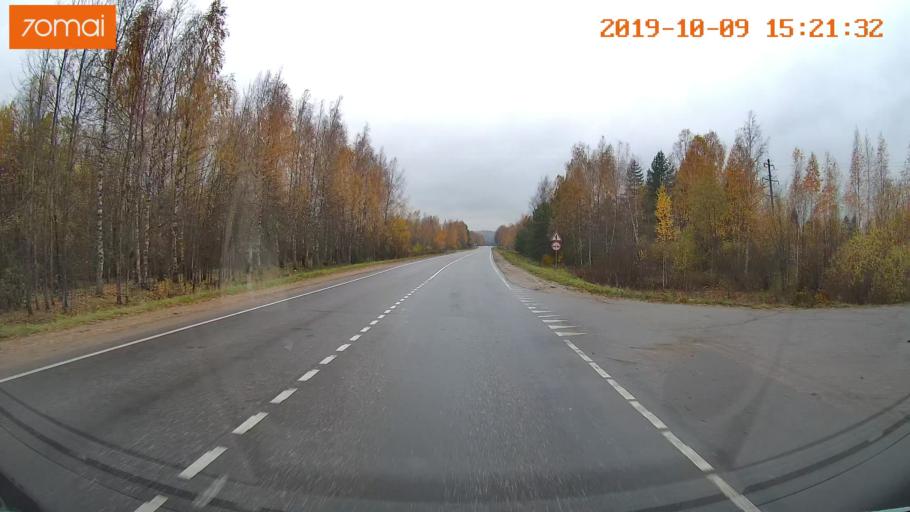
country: RU
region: Kostroma
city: Susanino
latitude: 58.0527
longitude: 41.5177
